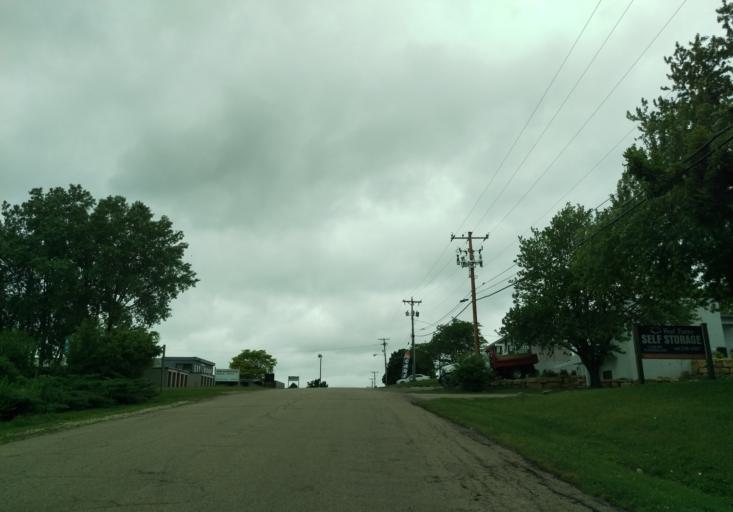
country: US
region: Wisconsin
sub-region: Dane County
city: Middleton
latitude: 43.0518
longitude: -89.4997
